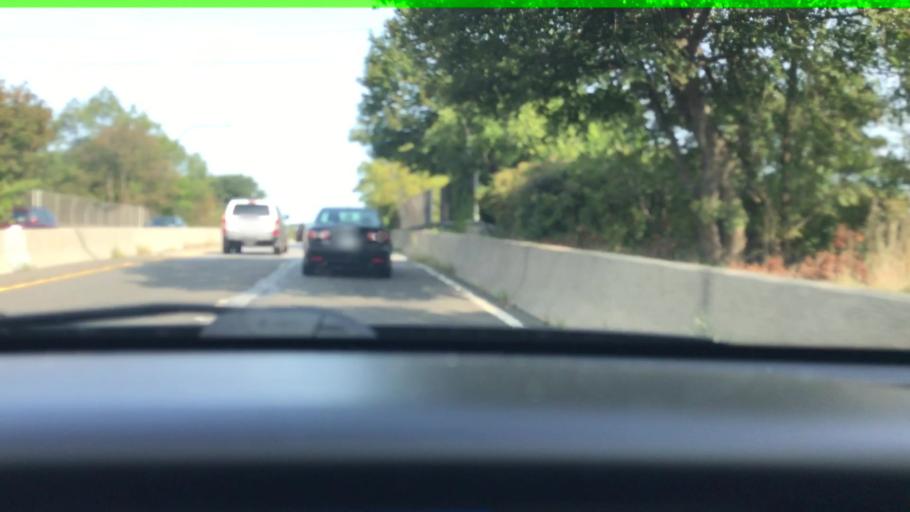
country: US
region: New York
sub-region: Nassau County
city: New Cassel
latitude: 40.7609
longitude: -73.5532
